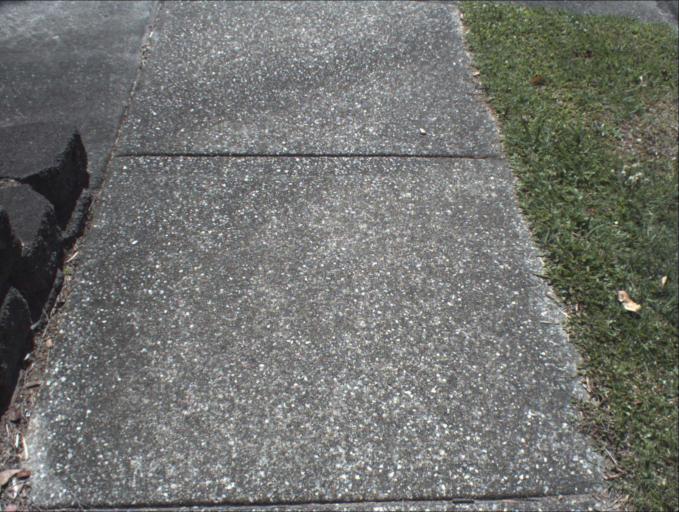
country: AU
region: Queensland
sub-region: Logan
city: Rochedale South
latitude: -27.5955
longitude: 153.1316
